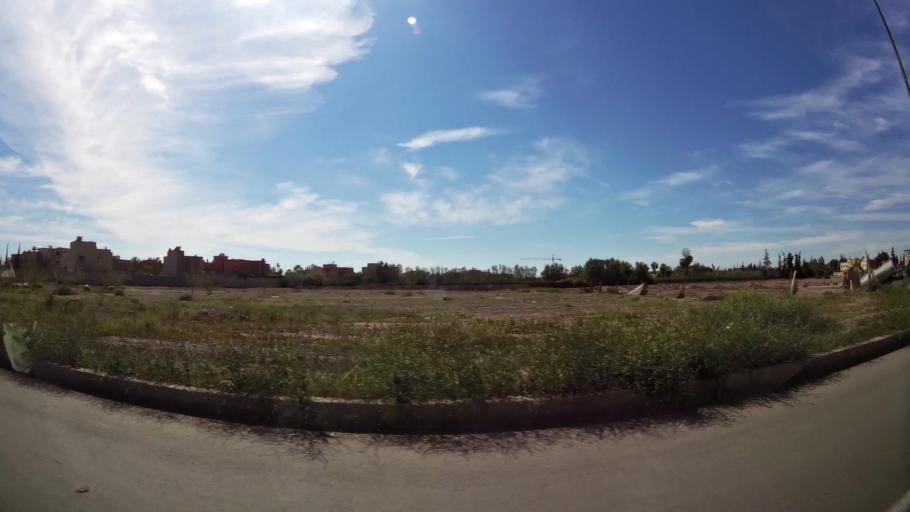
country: MA
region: Marrakech-Tensift-Al Haouz
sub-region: Marrakech
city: Marrakesh
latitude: 31.6541
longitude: -8.0601
